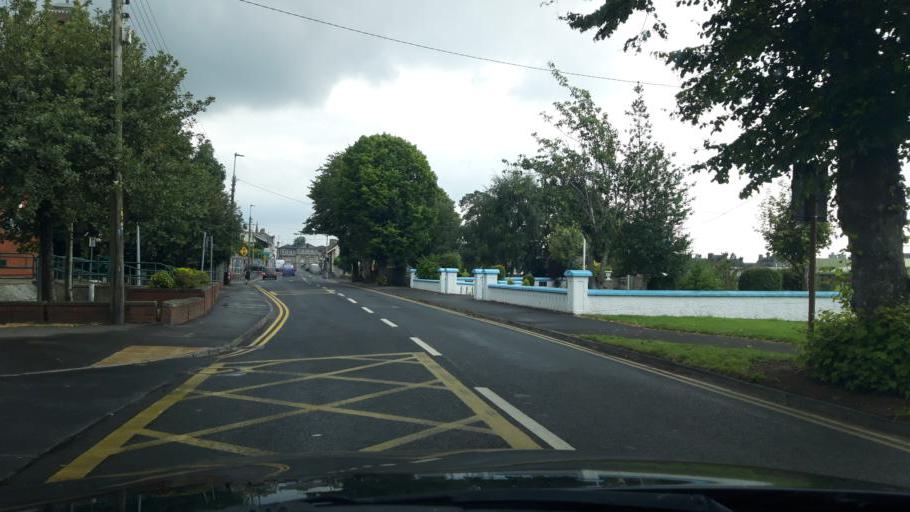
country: IE
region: Leinster
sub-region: Kildare
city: Athy
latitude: 52.9945
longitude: -6.9844
